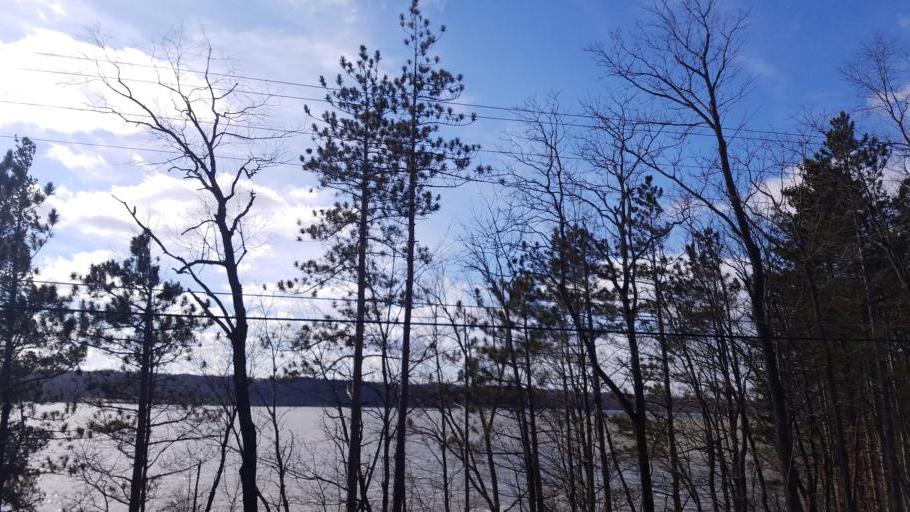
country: US
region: Ohio
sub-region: Richland County
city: Lexington
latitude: 40.7036
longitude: -82.6072
